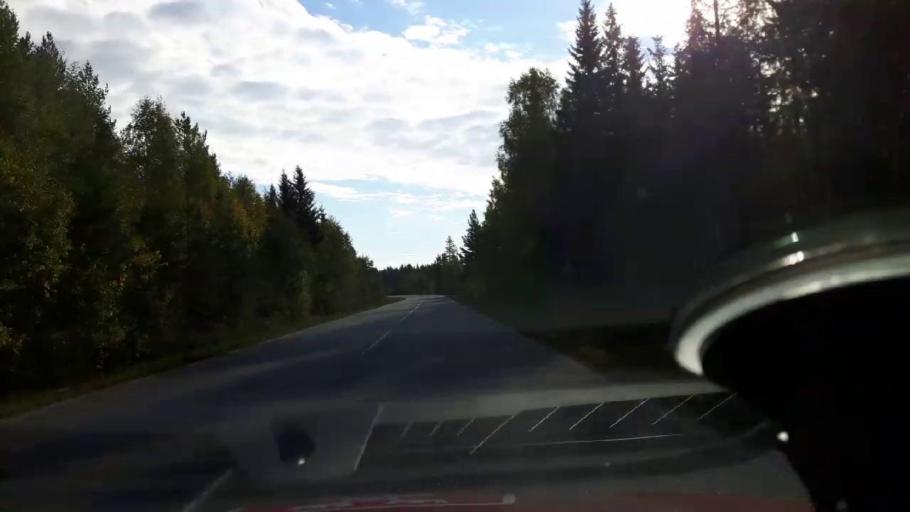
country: SE
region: Vaesternorrland
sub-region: Ange Kommun
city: Ange
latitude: 62.0472
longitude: 15.1587
